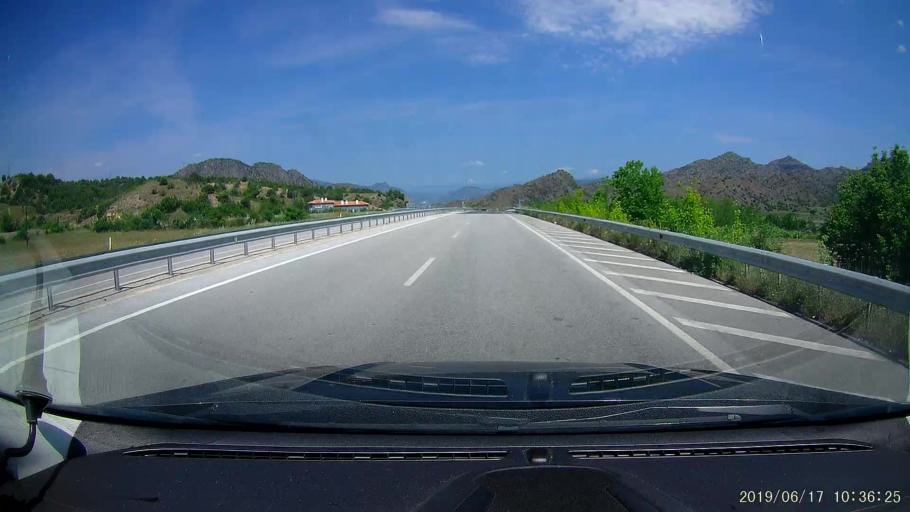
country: TR
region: Corum
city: Osmancik
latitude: 40.9789
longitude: 34.6815
